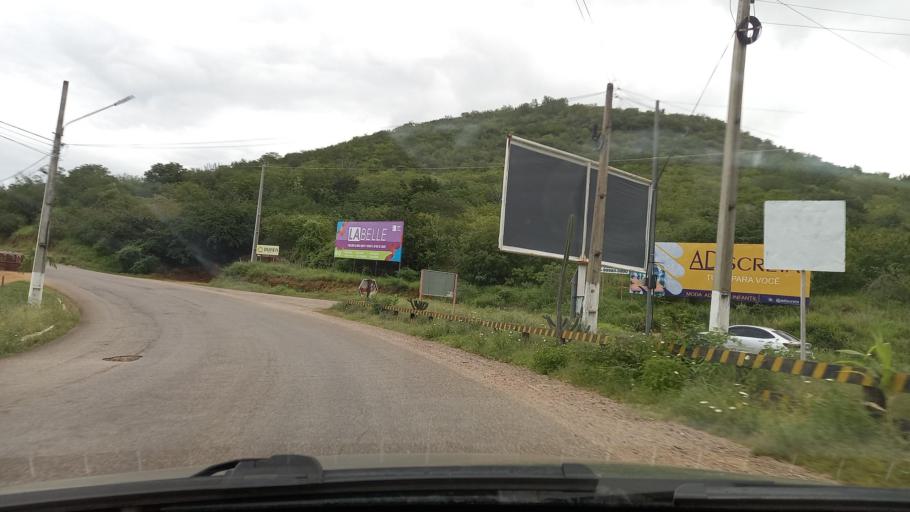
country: BR
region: Sergipe
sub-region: Caninde De Sao Francisco
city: Caninde de Sao Francisco
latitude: -9.6330
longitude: -37.7743
